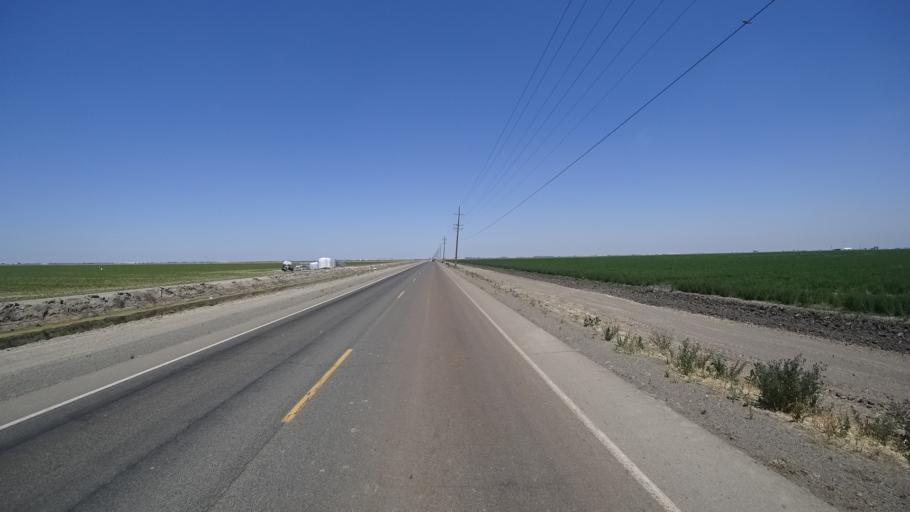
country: US
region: California
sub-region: Kings County
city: Corcoran
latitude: 36.1478
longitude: -119.6458
